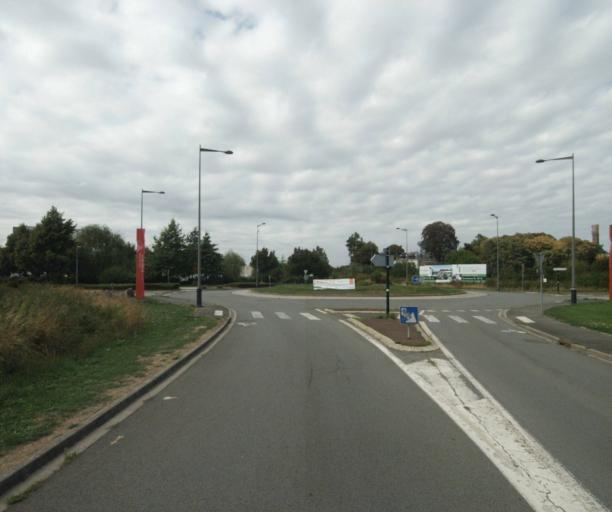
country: FR
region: Nord-Pas-de-Calais
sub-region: Departement du Nord
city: Villeneuve-d'Ascq
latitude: 50.6061
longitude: 3.1640
